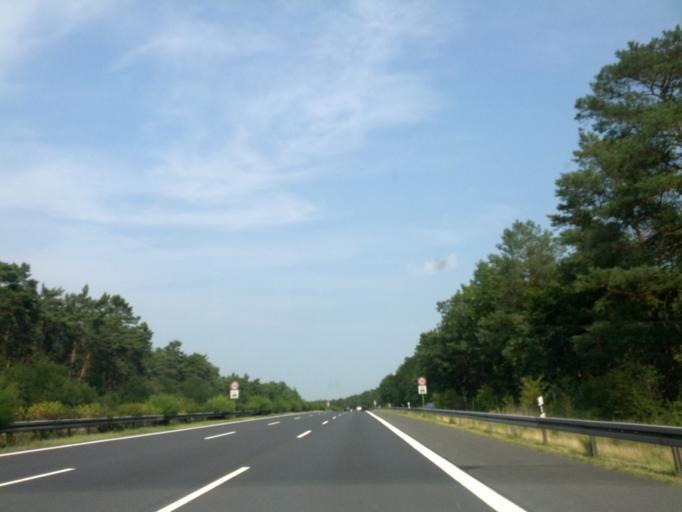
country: DE
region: Brandenburg
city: Borkheide
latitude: 52.2249
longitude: 12.9099
